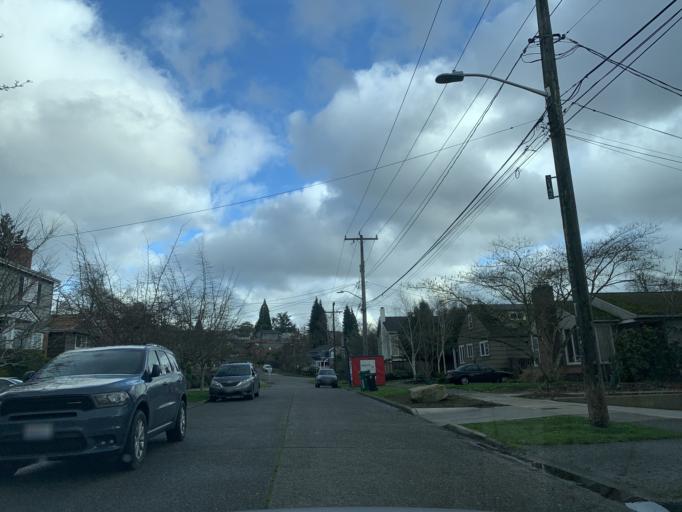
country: US
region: Washington
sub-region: King County
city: Yarrow Point
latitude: 47.6721
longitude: -122.2808
